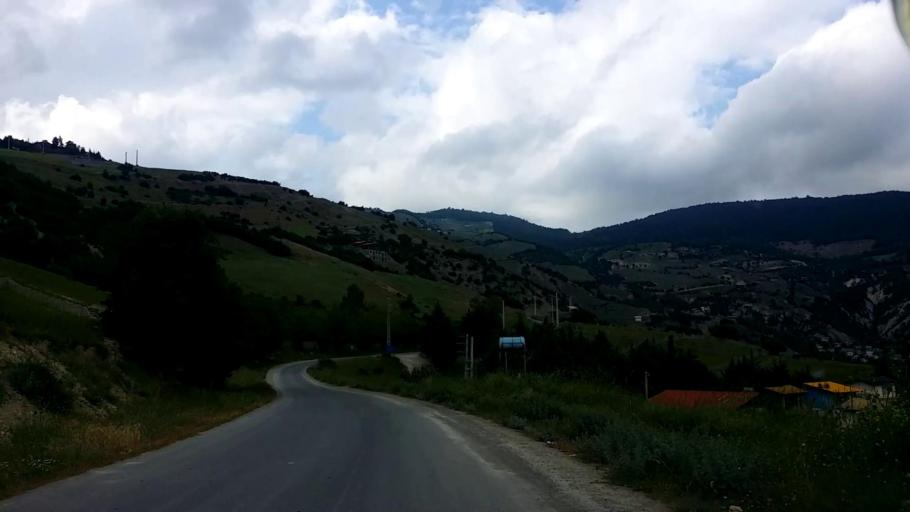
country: IR
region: Mazandaran
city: Chalus
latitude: 36.5433
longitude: 51.2718
